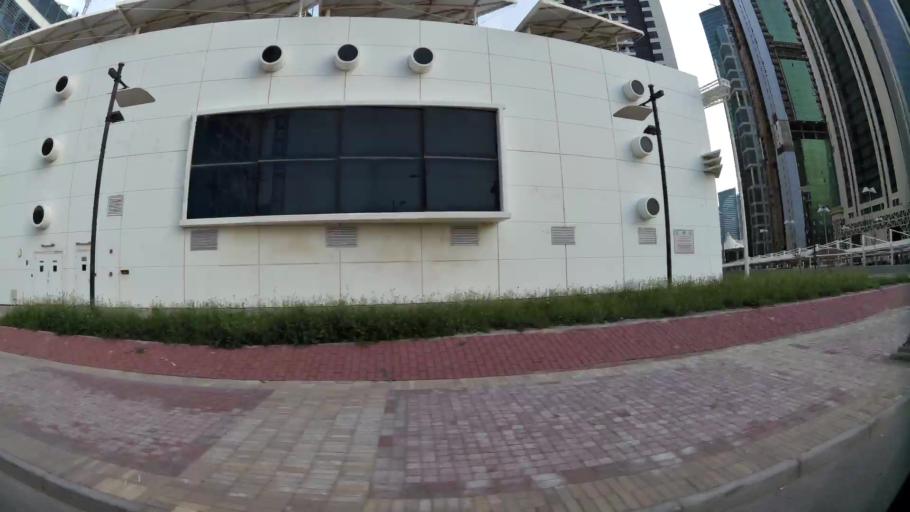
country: QA
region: Baladiyat ad Dawhah
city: Doha
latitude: 25.3296
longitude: 51.5319
